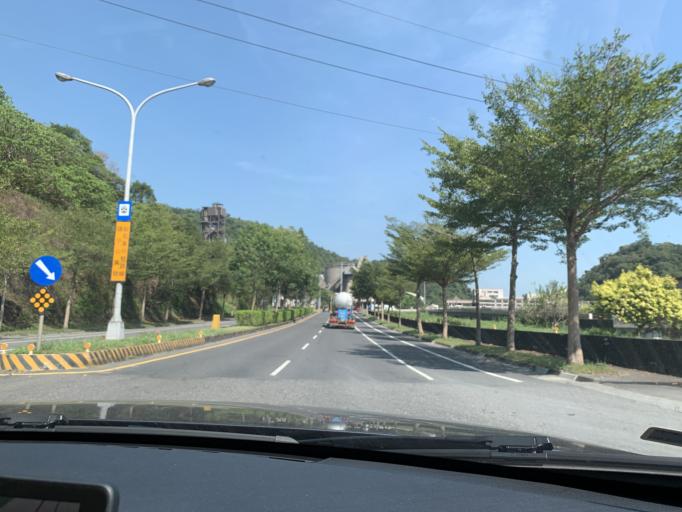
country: TW
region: Taiwan
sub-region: Yilan
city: Yilan
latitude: 24.6059
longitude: 121.8293
